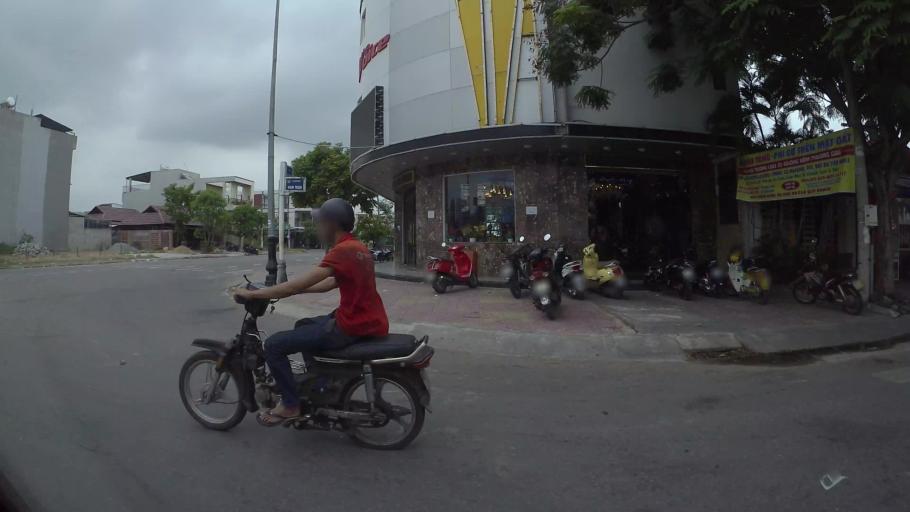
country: VN
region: Da Nang
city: Lien Chieu
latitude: 16.0624
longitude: 108.1711
